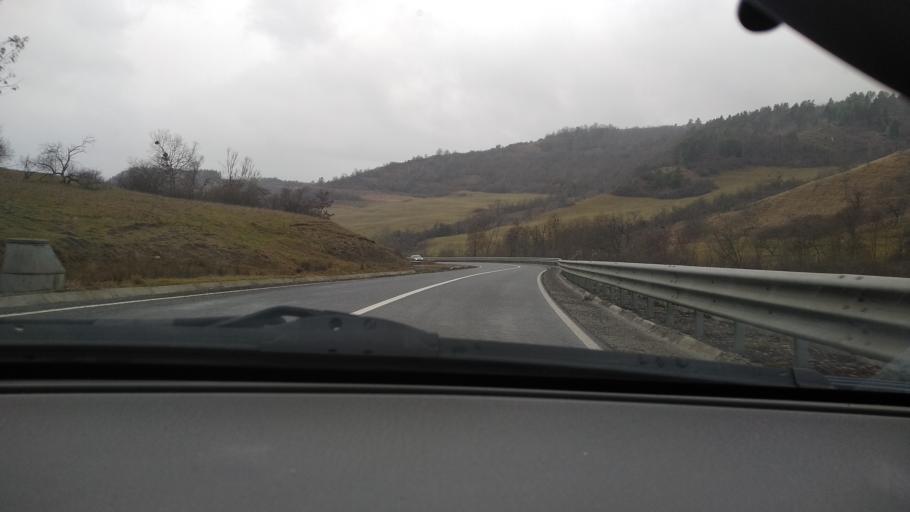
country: RO
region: Mures
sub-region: Comuna Magherani
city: Magherani
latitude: 46.5823
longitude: 24.9410
